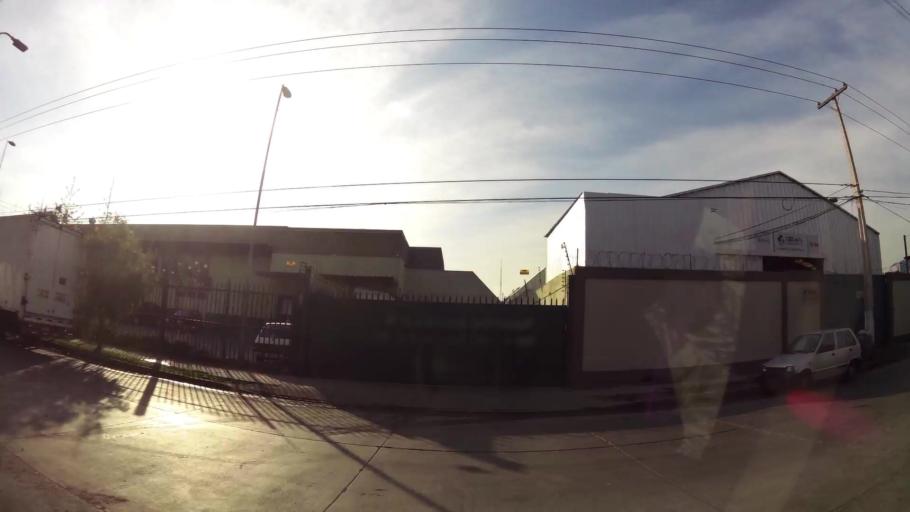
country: CL
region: Santiago Metropolitan
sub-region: Provincia de Santiago
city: Santiago
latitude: -33.5223
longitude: -70.6753
